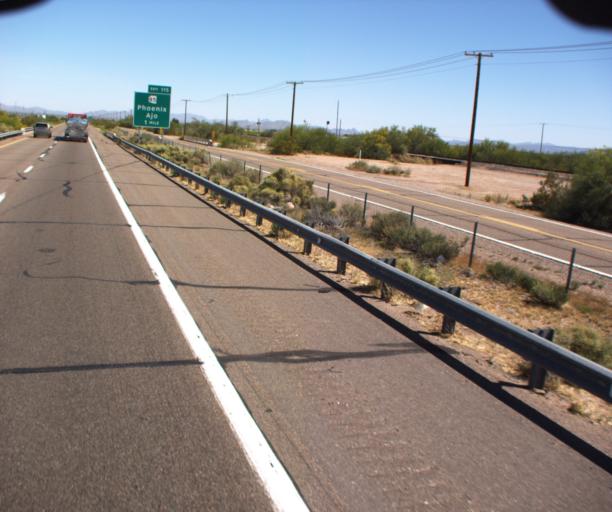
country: US
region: Arizona
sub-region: Maricopa County
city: Gila Bend
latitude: 32.9364
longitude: -112.7741
